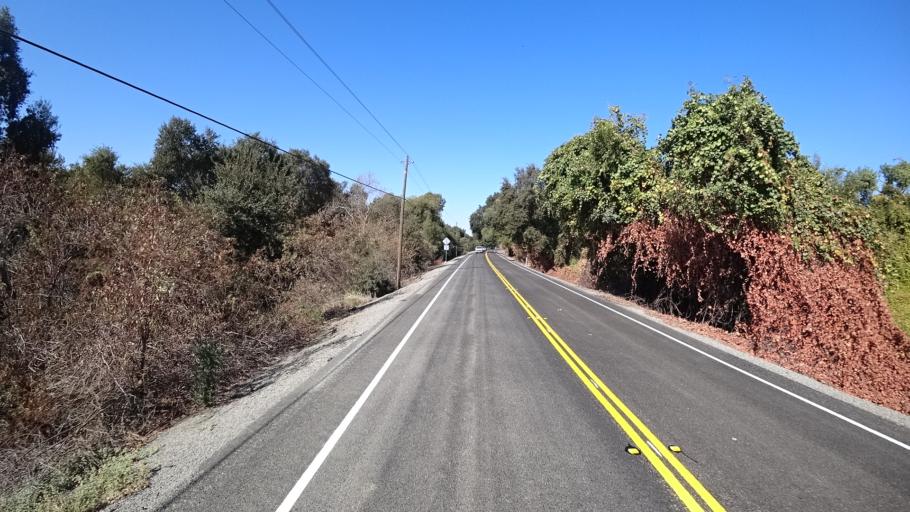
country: US
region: California
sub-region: Yolo County
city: West Sacramento
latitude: 38.6510
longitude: -121.6034
